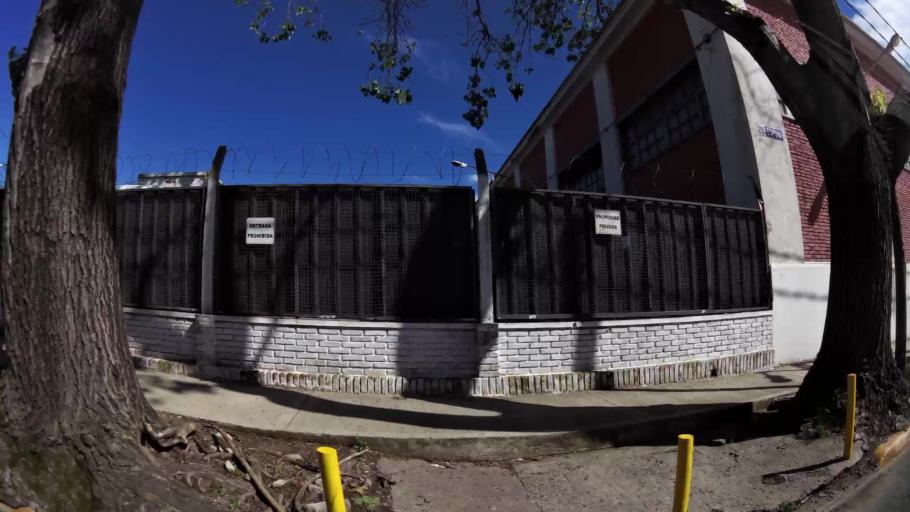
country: AR
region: Buenos Aires
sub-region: Partido de Quilmes
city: Quilmes
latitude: -34.7075
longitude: -58.2812
